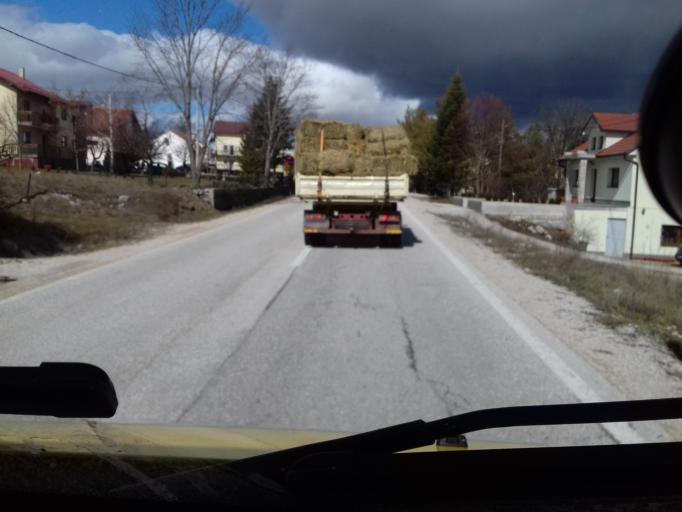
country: BA
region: Federation of Bosnia and Herzegovina
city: Dreznica
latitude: 43.6061
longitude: 17.2719
